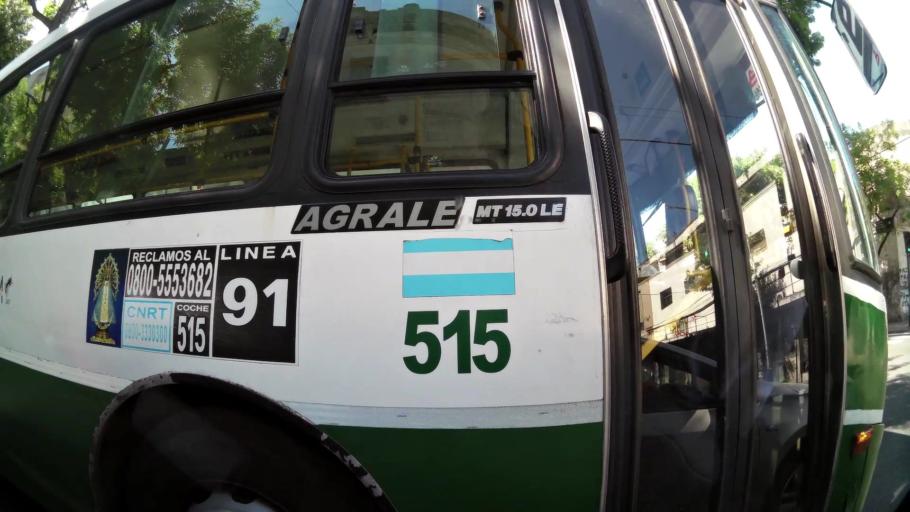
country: AR
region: Buenos Aires F.D.
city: Buenos Aires
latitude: -34.6310
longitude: -58.3841
